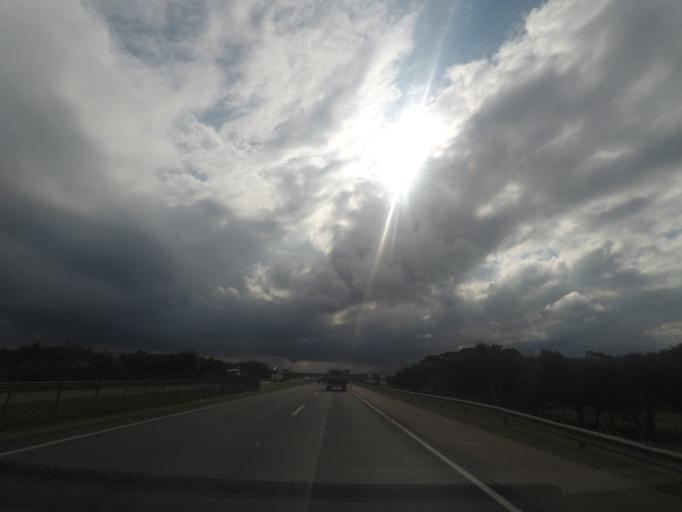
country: BR
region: Parana
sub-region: Sao Jose Dos Pinhais
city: Sao Jose dos Pinhais
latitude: -25.5006
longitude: -49.1523
